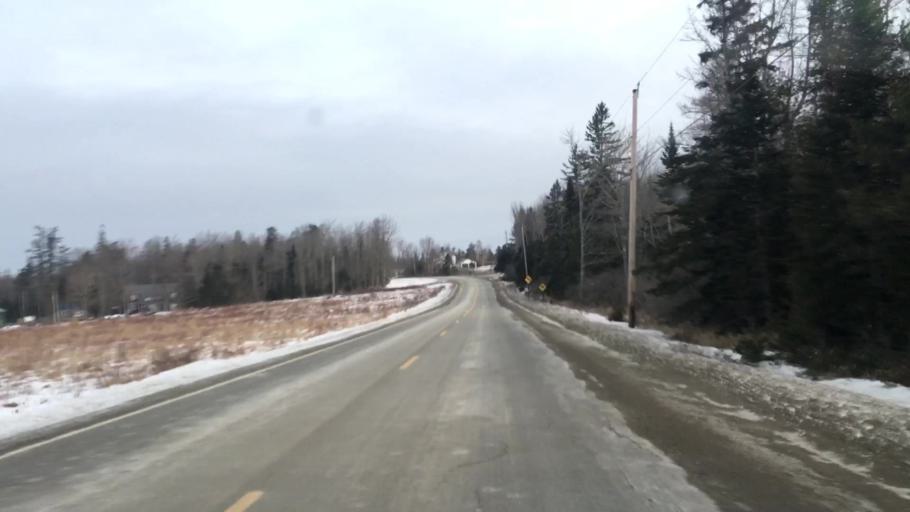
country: US
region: Maine
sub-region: Hancock County
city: Franklin
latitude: 44.7217
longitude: -68.3349
